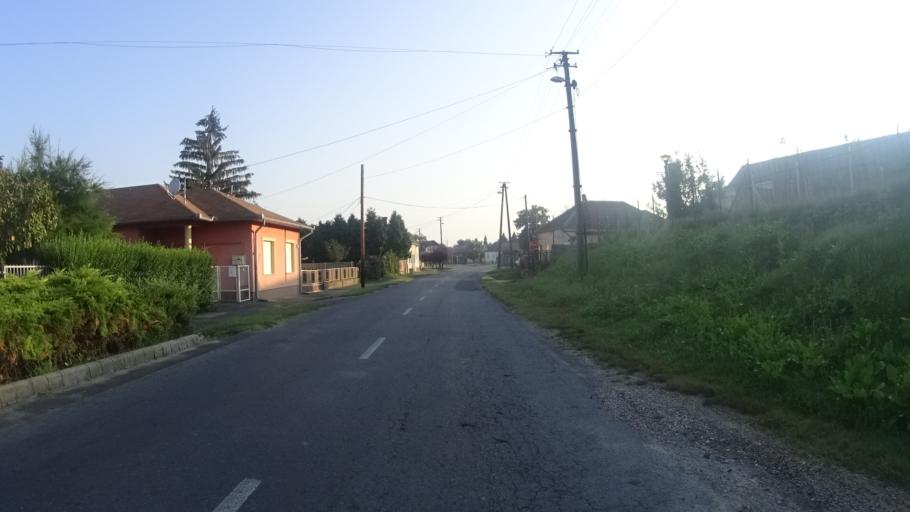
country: HU
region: Zala
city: Zalakomar
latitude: 46.5474
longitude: 17.1743
